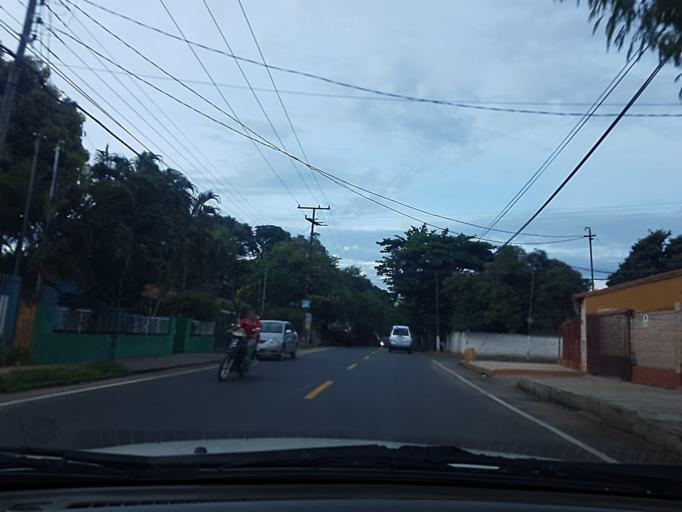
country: PY
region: Central
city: San Lorenzo
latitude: -25.2691
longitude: -57.4751
